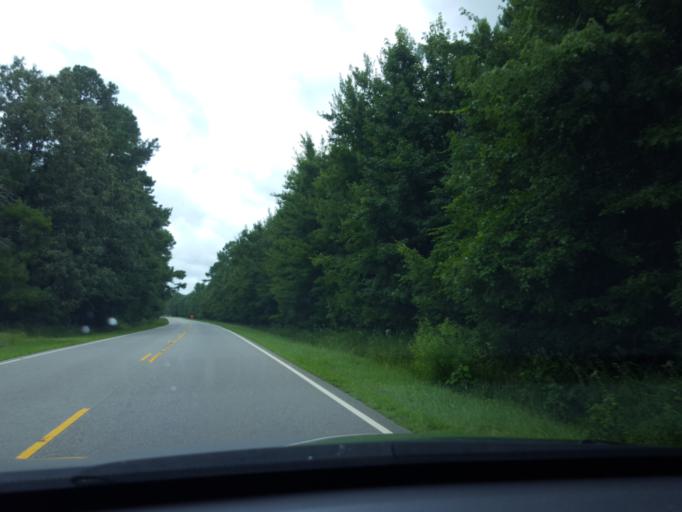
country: US
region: North Carolina
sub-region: Beaufort County
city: Washington
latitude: 35.6803
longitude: -76.9955
